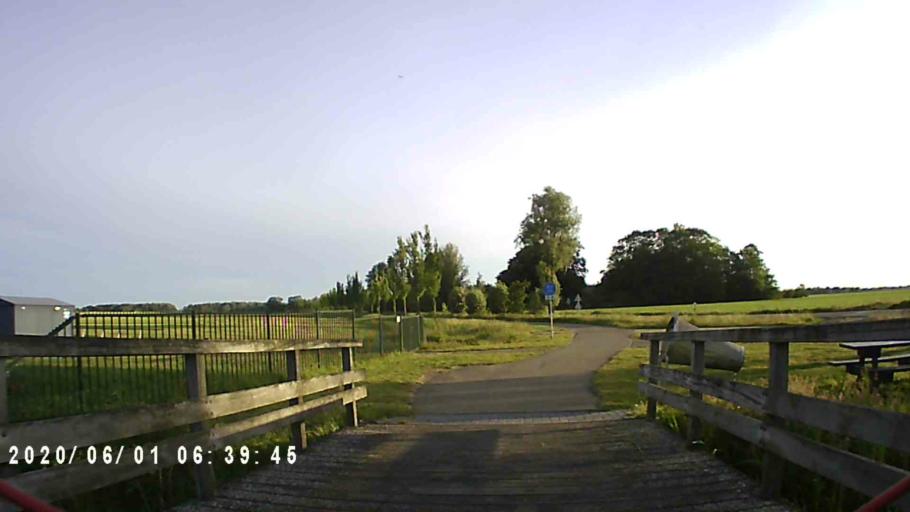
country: NL
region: Friesland
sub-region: Gemeente Kollumerland en Nieuwkruisland
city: Kollum
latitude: 53.2909
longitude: 6.1587
